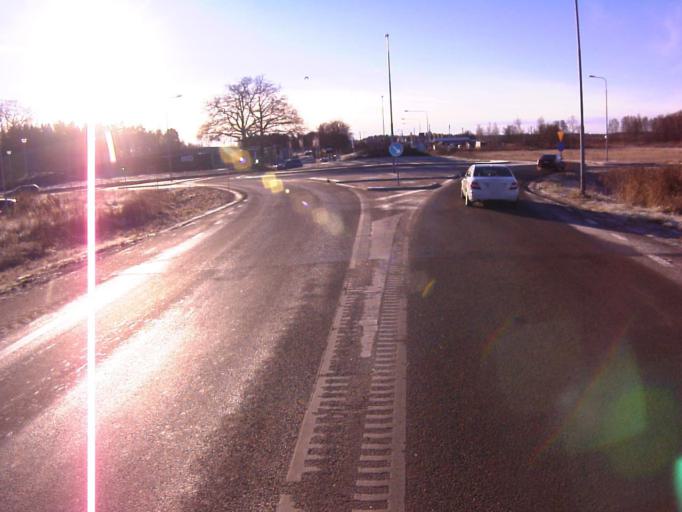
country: SE
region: Soedermanland
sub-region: Eskilstuna Kommun
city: Torshalla
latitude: 59.3970
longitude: 16.4704
